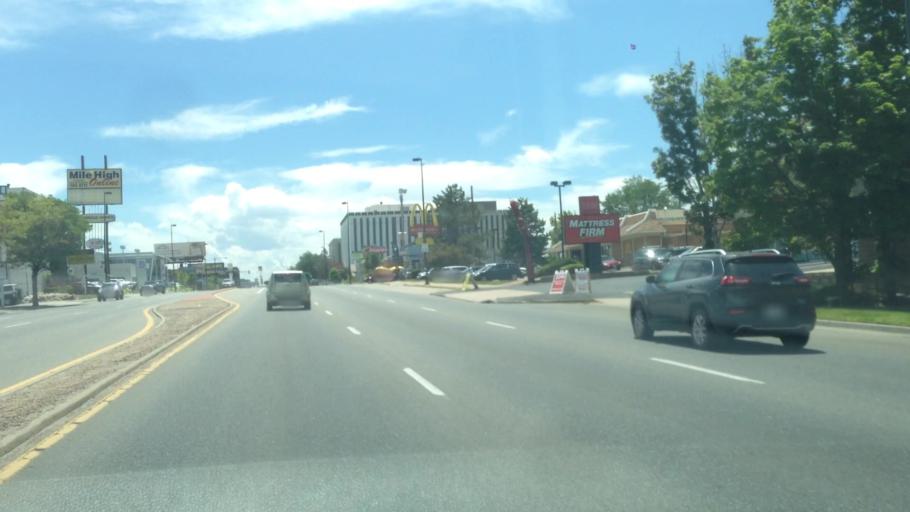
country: US
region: Colorado
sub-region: Arapahoe County
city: Glendale
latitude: 39.6960
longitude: -104.9407
